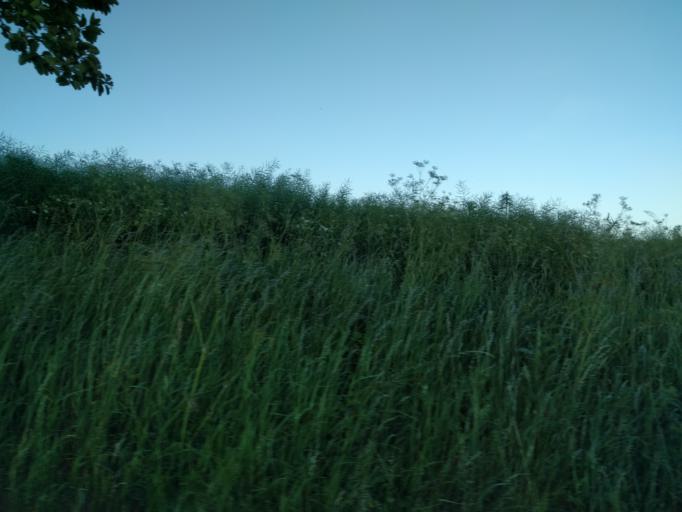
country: DK
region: South Denmark
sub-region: Kerteminde Kommune
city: Kerteminde
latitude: 55.5926
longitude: 10.6287
